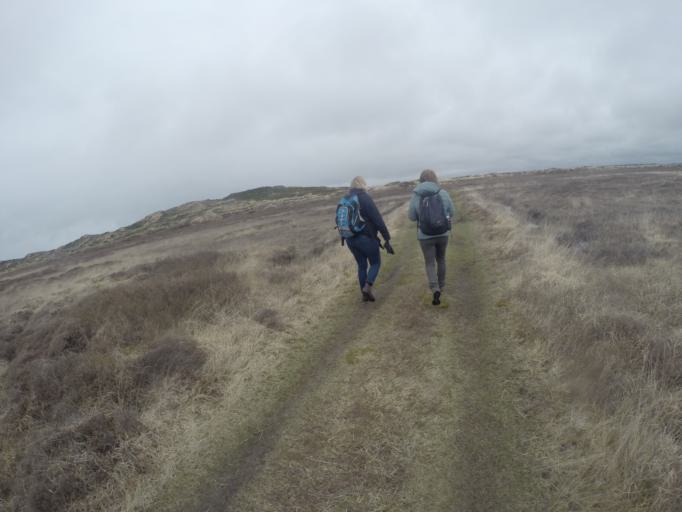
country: DK
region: North Denmark
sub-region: Thisted Kommune
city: Hurup
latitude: 56.8551
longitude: 8.2897
